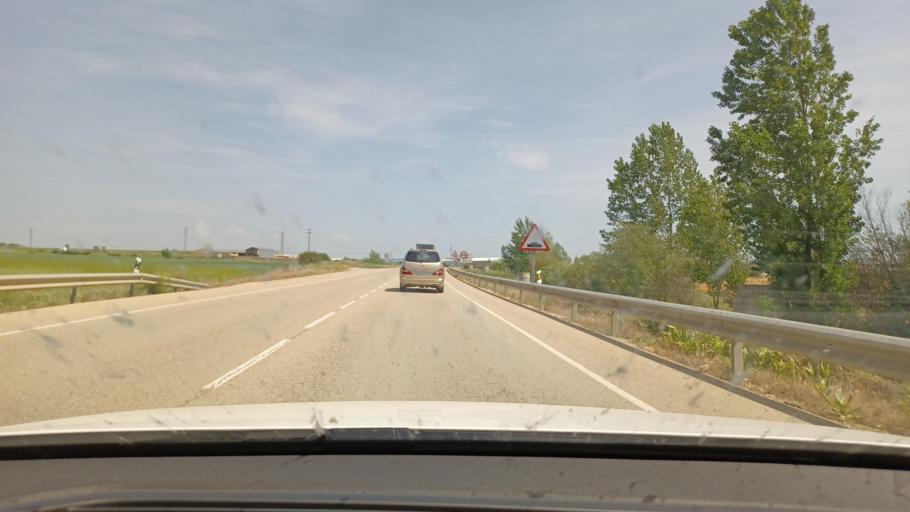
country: ES
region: Castille and Leon
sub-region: Provincia de Soria
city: Almazan
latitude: 41.4727
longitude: -2.5434
